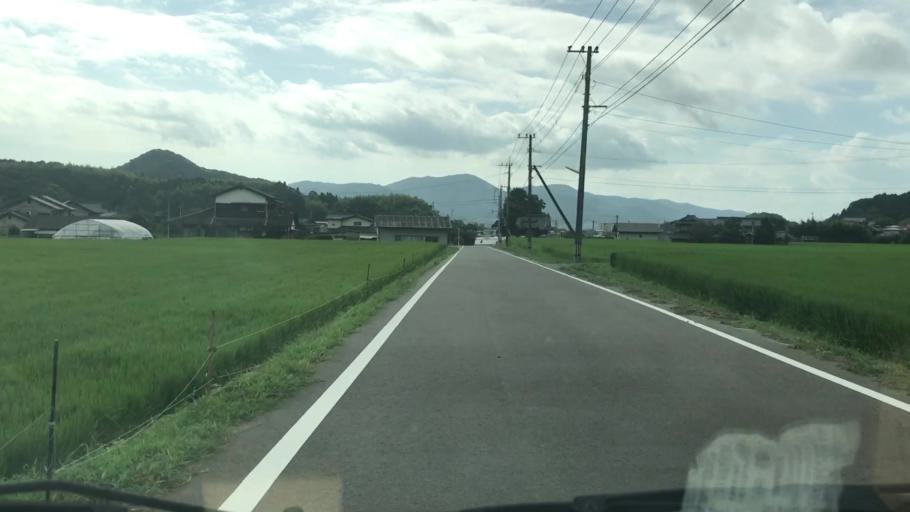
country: JP
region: Saga Prefecture
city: Takeocho-takeo
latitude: 33.2269
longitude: 130.0213
